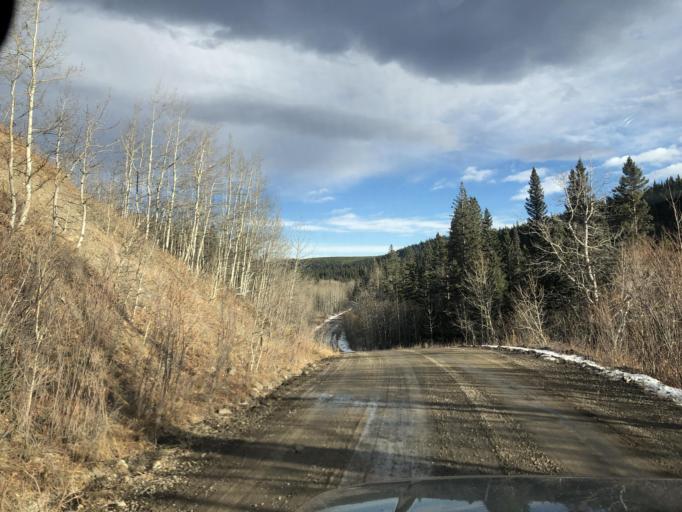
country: CA
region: Alberta
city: Cochrane
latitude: 51.0229
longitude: -114.8909
